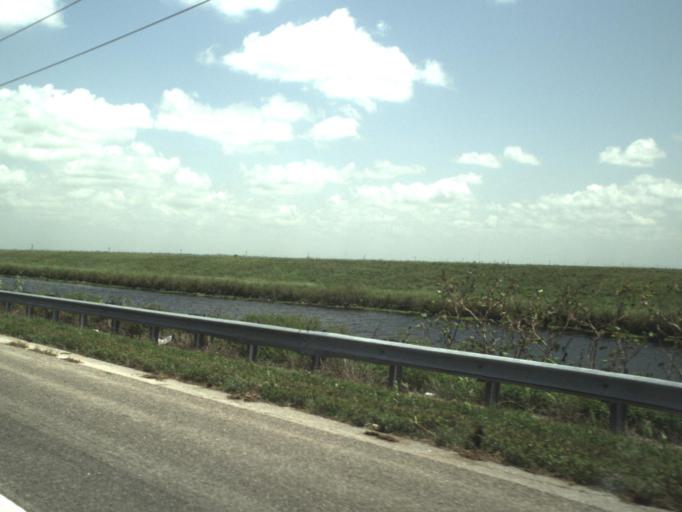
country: US
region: Florida
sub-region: Palm Beach County
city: South Bay
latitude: 26.6001
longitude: -80.7112
